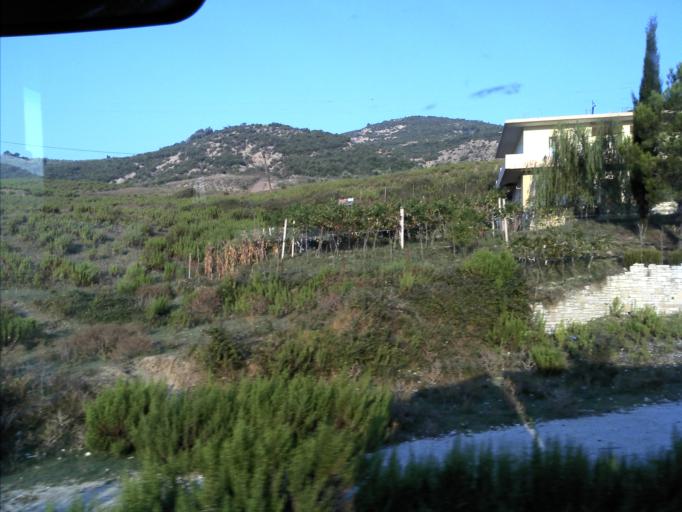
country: AL
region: Gjirokaster
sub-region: Rrethi i Tepelenes
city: Krahes
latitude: 40.4490
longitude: 19.8486
